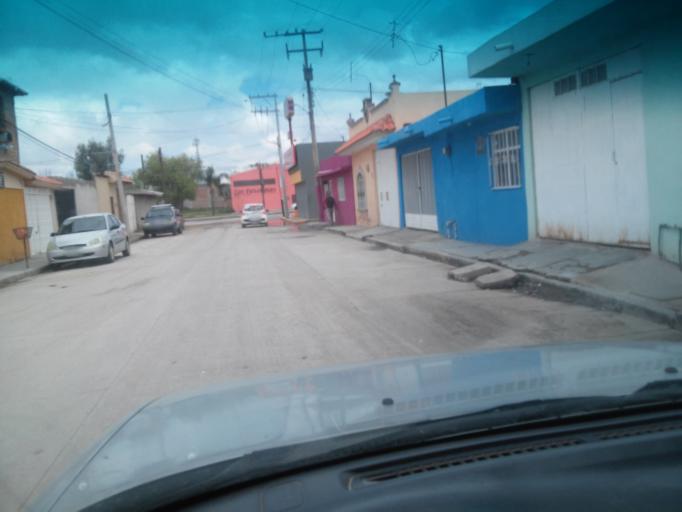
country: MX
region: Durango
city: Victoria de Durango
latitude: 24.0107
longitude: -104.6268
